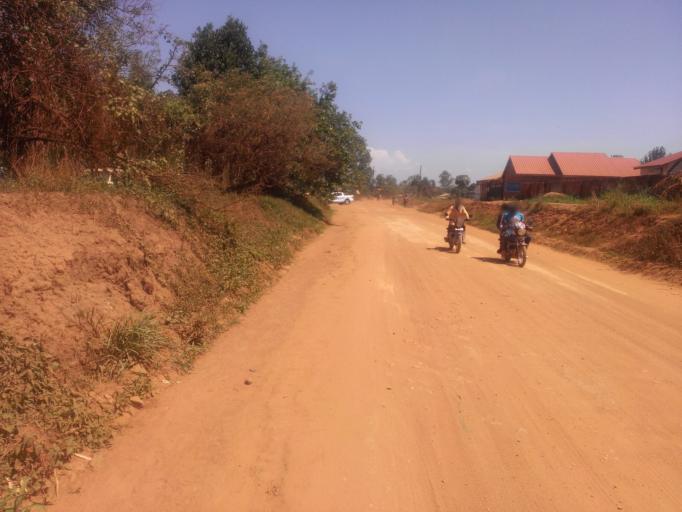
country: UG
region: Northern Region
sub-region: Gulu District
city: Gulu
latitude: 2.7821
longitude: 32.2944
